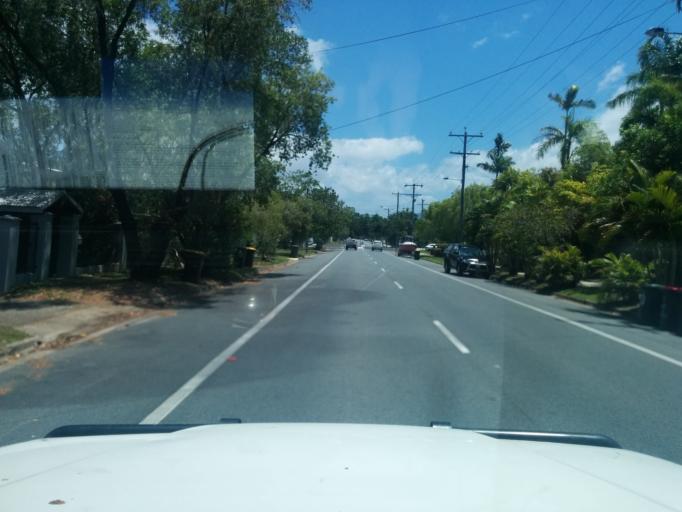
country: AU
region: Queensland
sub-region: Cairns
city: Cairns
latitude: -16.9020
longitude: 145.7442
